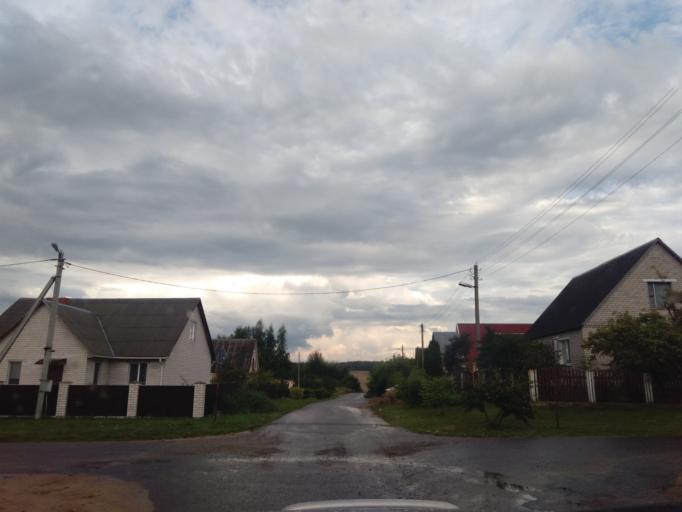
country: BY
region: Minsk
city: Kapyl'
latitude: 53.1667
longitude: 27.0873
